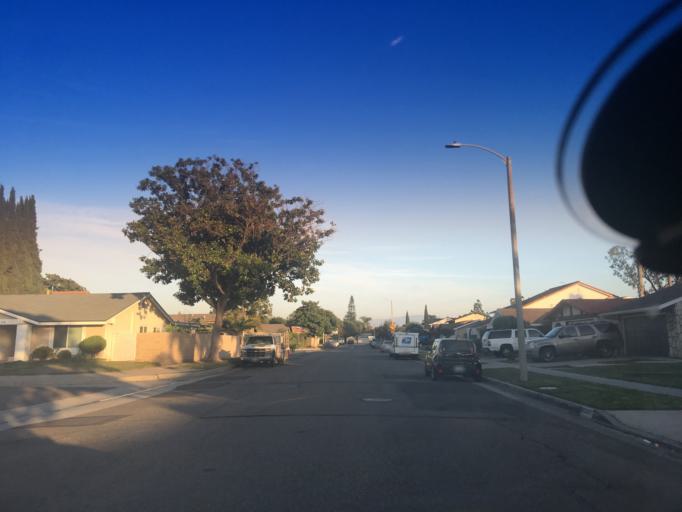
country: US
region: California
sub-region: Orange County
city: Anaheim
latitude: 33.8205
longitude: -117.8833
